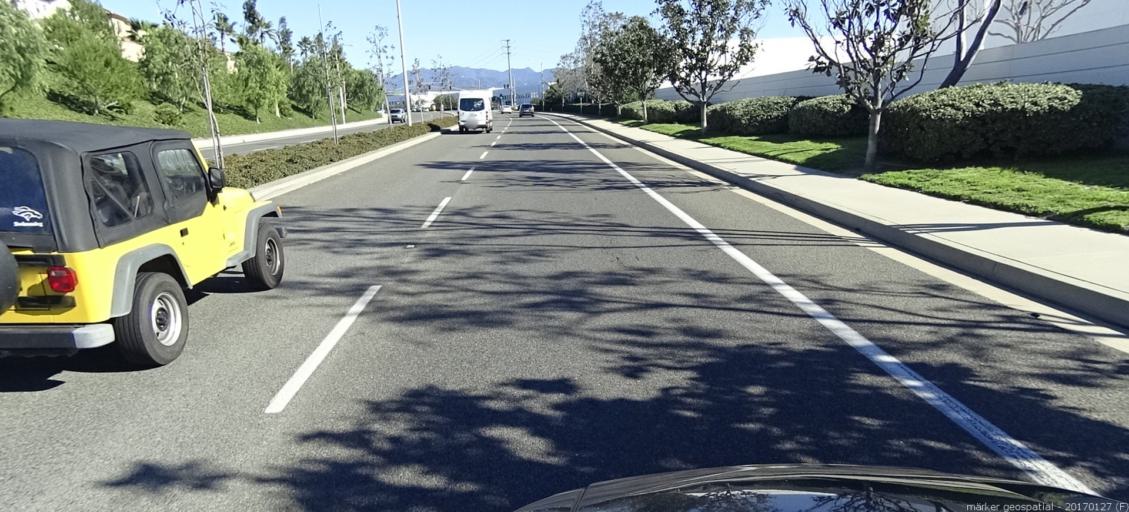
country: US
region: California
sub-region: Orange County
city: Lake Forest
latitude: 33.6676
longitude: -117.6782
